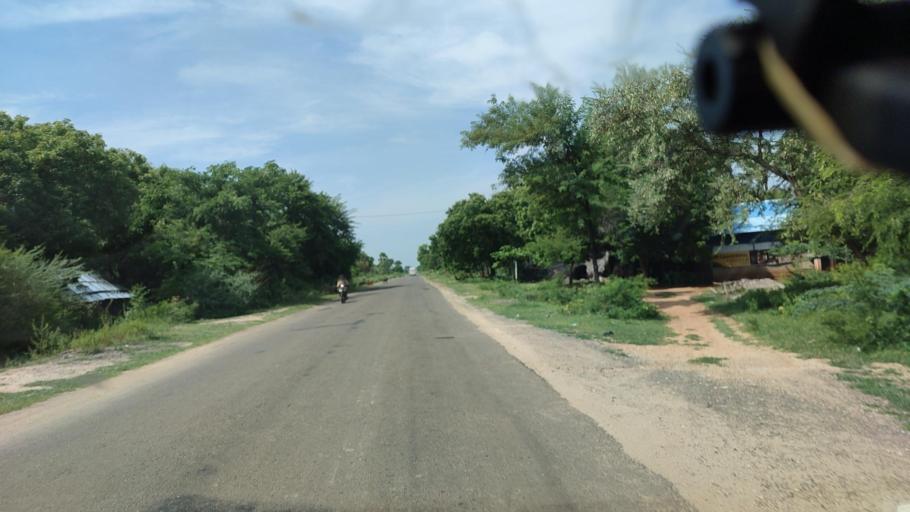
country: MM
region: Mandalay
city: Myingyan
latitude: 21.3585
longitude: 95.3221
